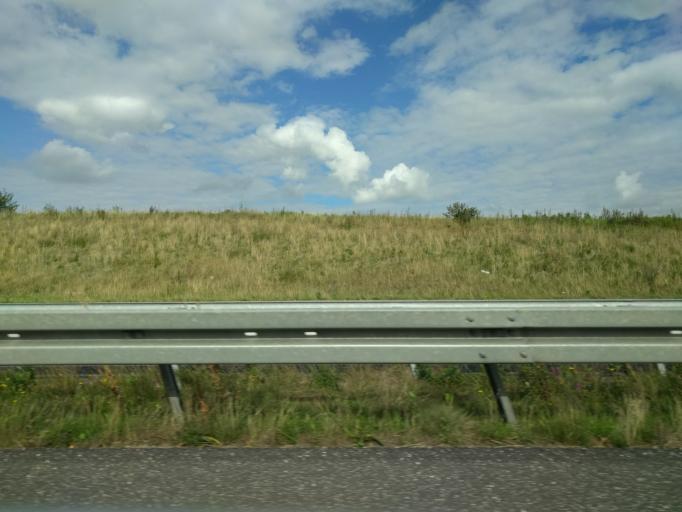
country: DK
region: Central Jutland
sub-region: Hedensted Kommune
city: Torring
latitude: 55.8251
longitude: 9.5344
